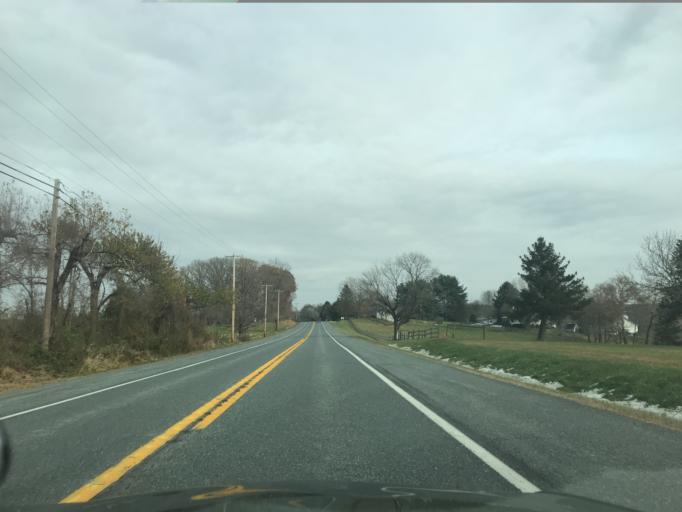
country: US
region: Maryland
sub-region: Harford County
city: Jarrettsville
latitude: 39.6540
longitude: -76.4614
